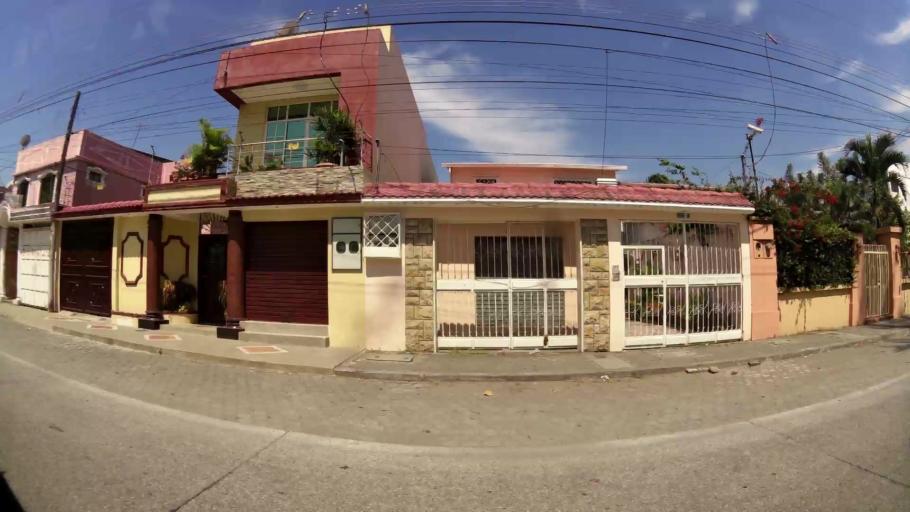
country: EC
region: Guayas
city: Eloy Alfaro
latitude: -2.1105
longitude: -79.9037
